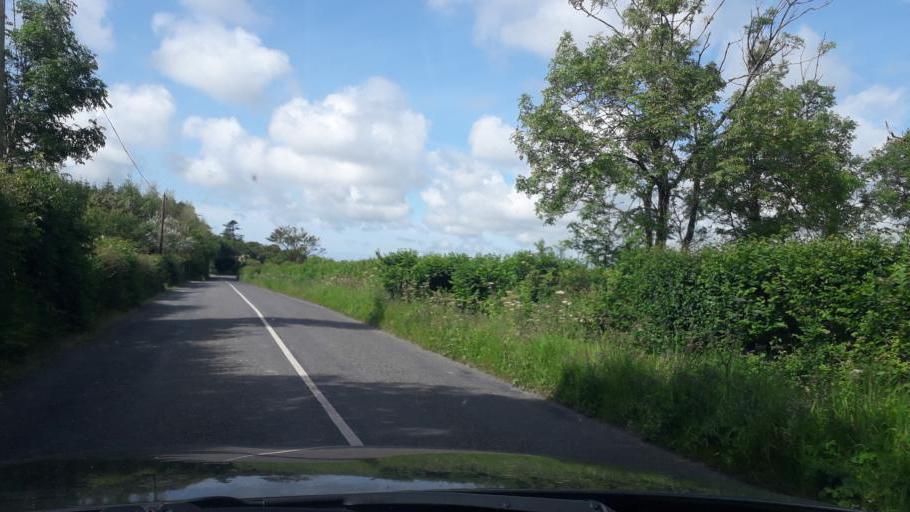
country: IE
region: Leinster
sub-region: Loch Garman
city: Loch Garman
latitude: 52.2789
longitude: -6.5408
